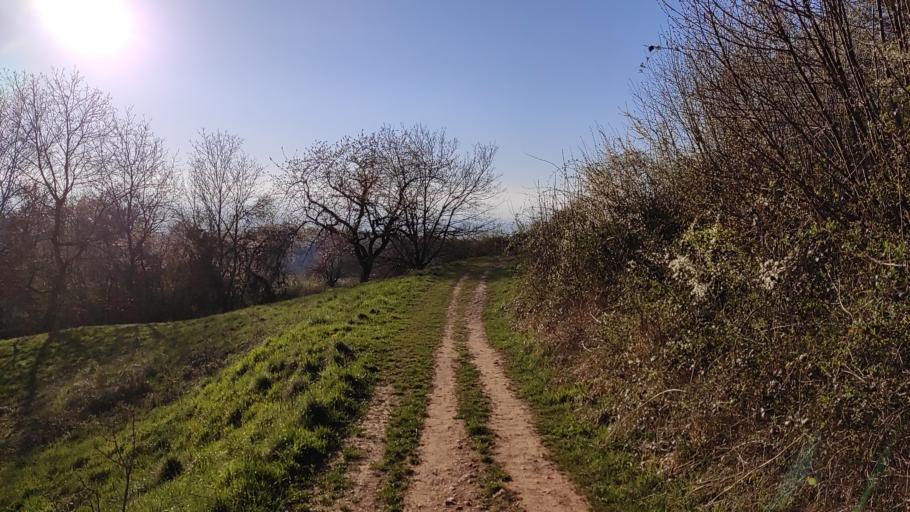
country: DE
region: Baden-Wuerttemberg
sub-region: Freiburg Region
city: Ebringen
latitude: 47.9488
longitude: 7.7951
